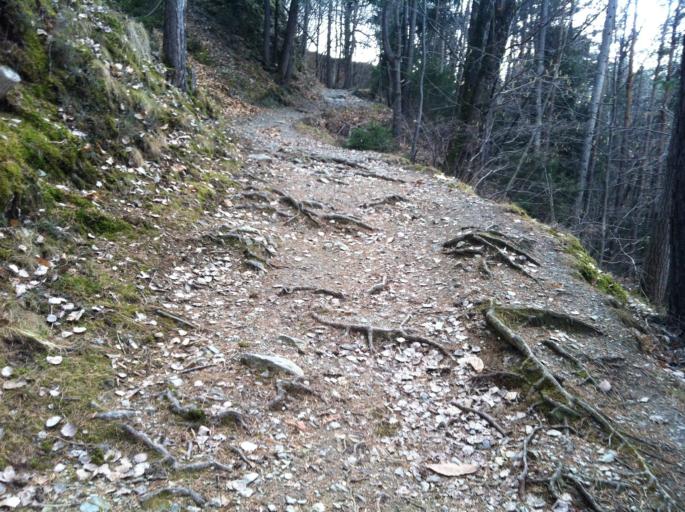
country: IT
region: Trentino-Alto Adige
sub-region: Bolzano
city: Bressanone
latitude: 46.6993
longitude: 11.6643
